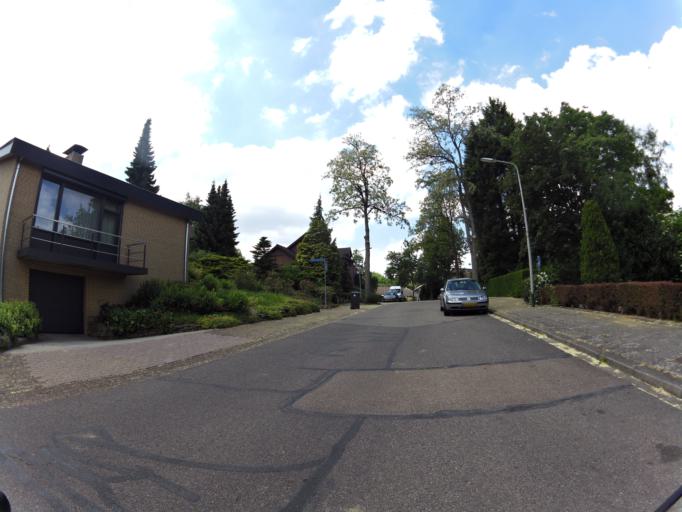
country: NL
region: Limburg
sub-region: Gemeente Kerkrade
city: Kerkrade
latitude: 50.8828
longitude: 6.0712
